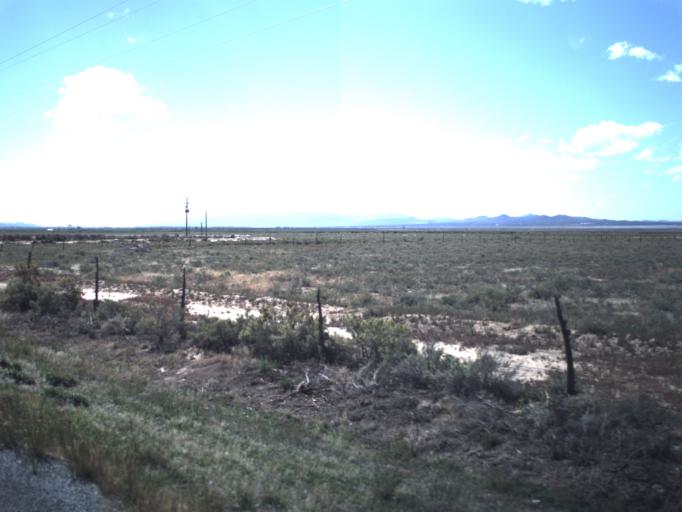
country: US
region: Utah
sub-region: Iron County
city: Enoch
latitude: 37.8771
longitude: -113.0316
